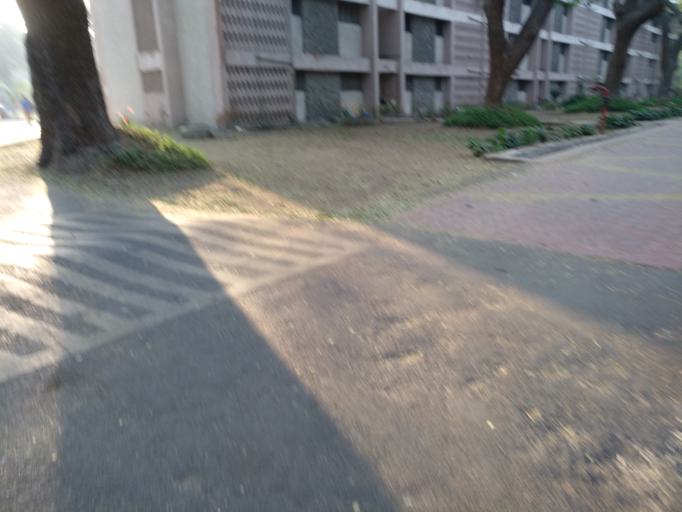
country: IN
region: Maharashtra
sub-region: Mumbai Suburban
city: Mumbai
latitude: 19.0395
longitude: 72.9251
